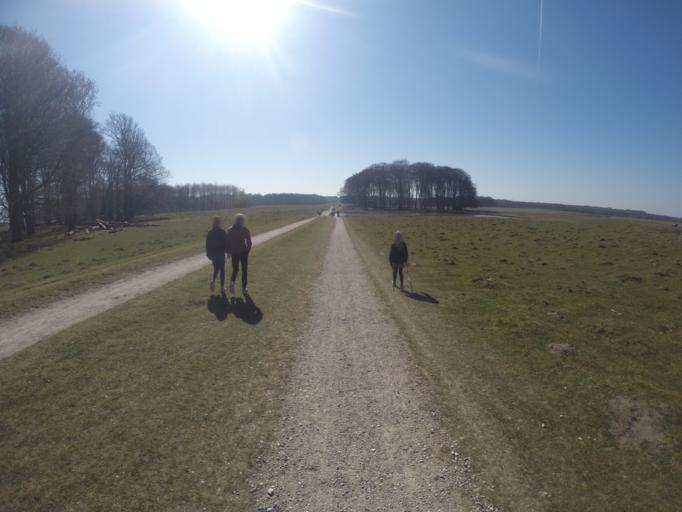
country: DK
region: Capital Region
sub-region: Gentofte Kommune
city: Charlottenlund
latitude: 55.7945
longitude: 12.5704
